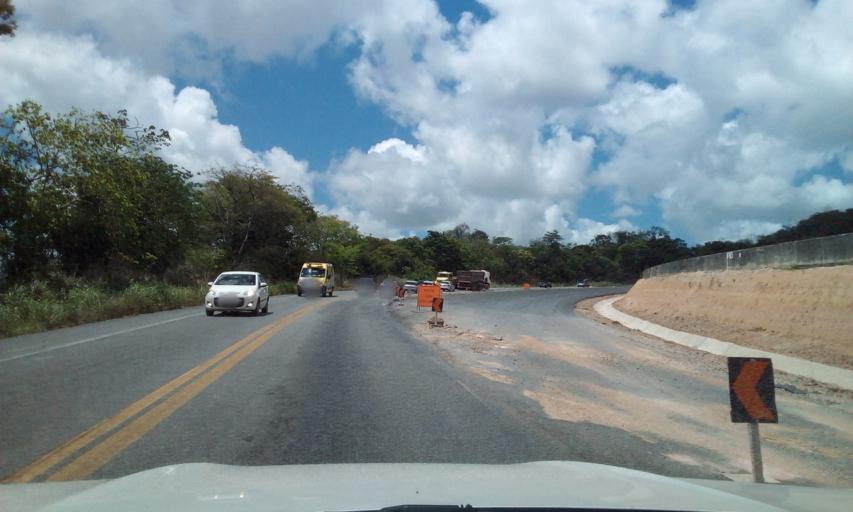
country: BR
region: Alagoas
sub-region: Sao Miguel Dos Campos
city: Sao Miguel dos Campos
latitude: -9.8873
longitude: -36.1374
